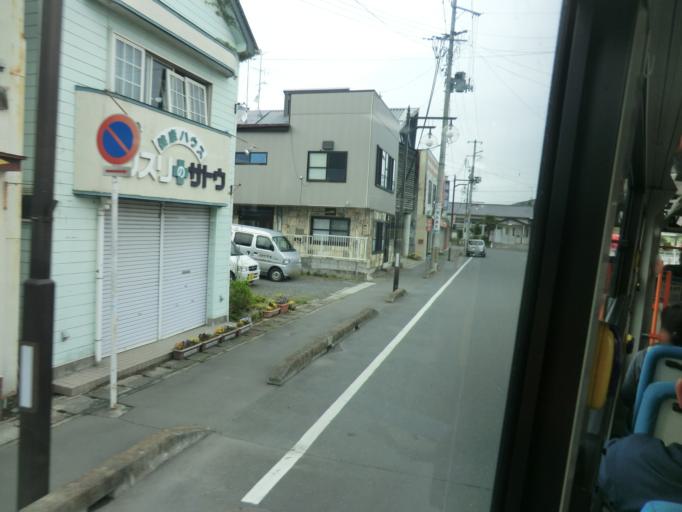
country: JP
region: Miyagi
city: Wakuya
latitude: 38.5116
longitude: 141.1933
